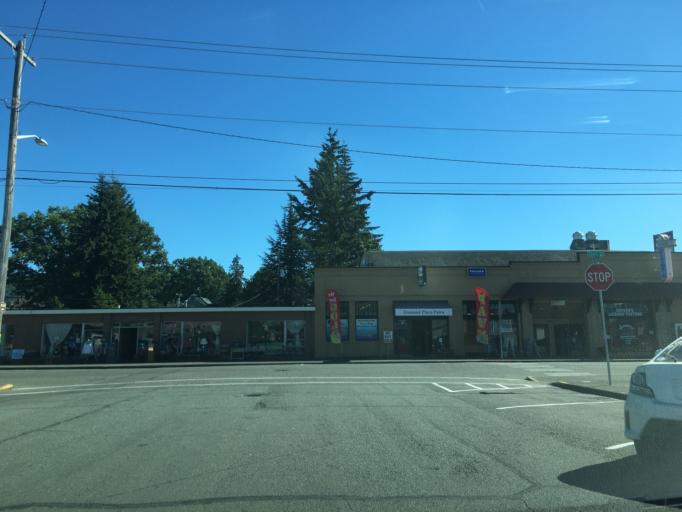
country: US
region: Washington
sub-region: Skagit County
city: Sedro-Woolley
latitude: 48.5036
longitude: -122.2368
